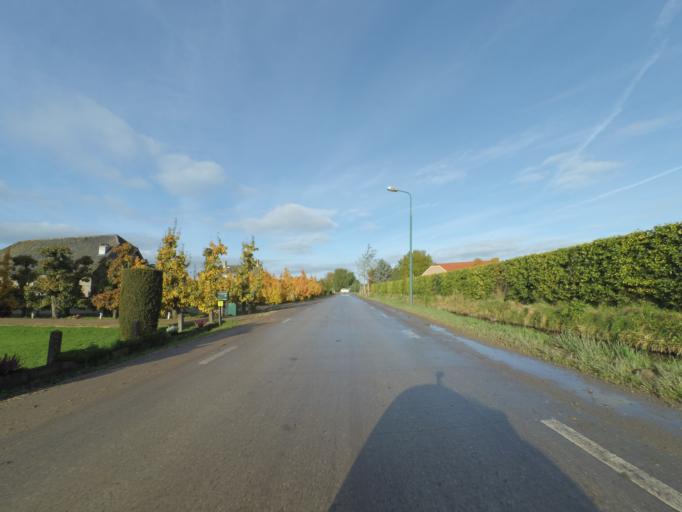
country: NL
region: Utrecht
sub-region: Gemeente Wijk bij Duurstede
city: Wijk bij Duurstede
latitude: 51.9785
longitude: 5.3136
